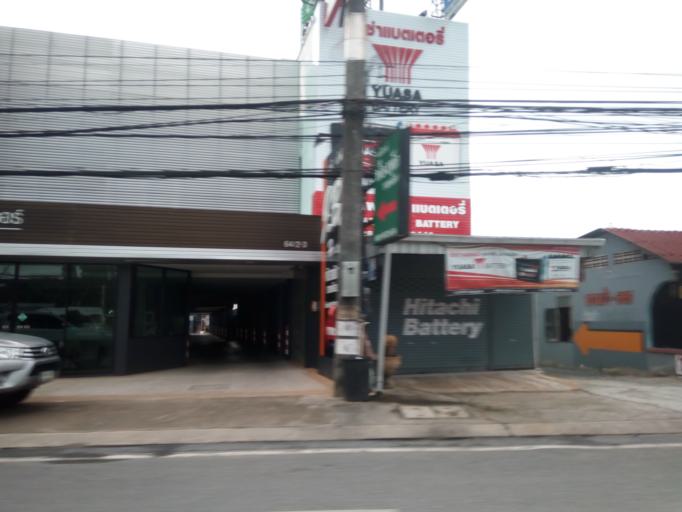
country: TH
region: Phuket
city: Thalang
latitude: 8.0321
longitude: 98.3331
